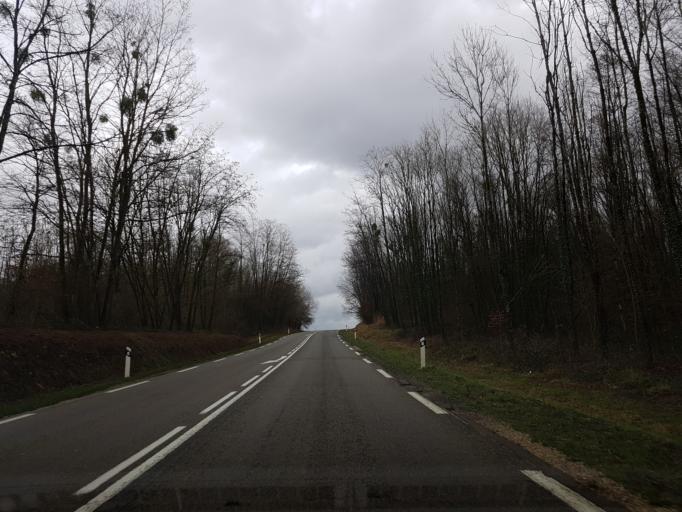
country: FR
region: Franche-Comte
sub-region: Departement de la Haute-Saone
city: Jussey
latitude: 47.7201
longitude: 5.8647
